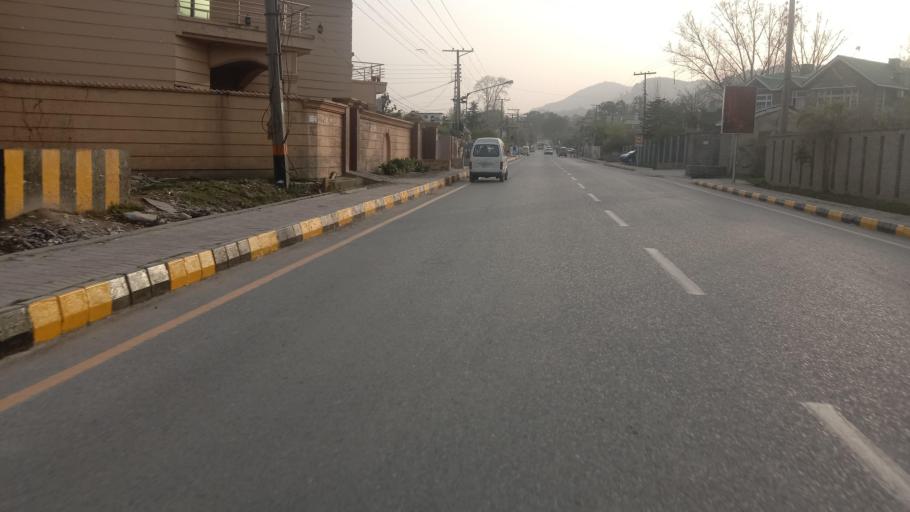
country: PK
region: Khyber Pakhtunkhwa
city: Abbottabad
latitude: 34.1682
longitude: 73.2291
